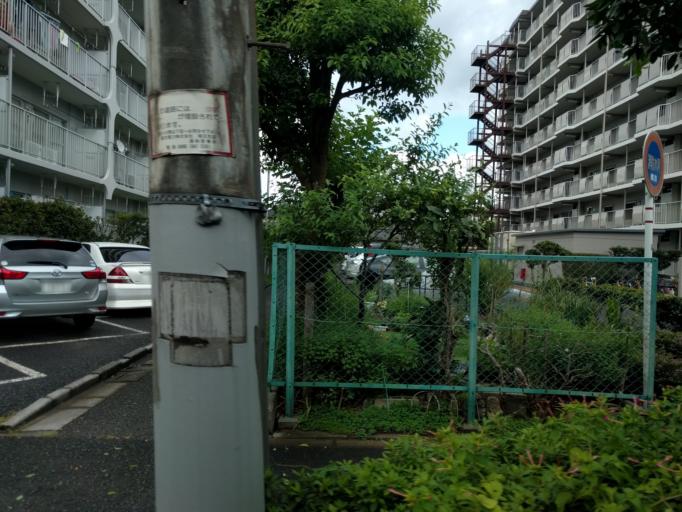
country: JP
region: Saitama
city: Shimotoda
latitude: 35.8344
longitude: 139.6704
